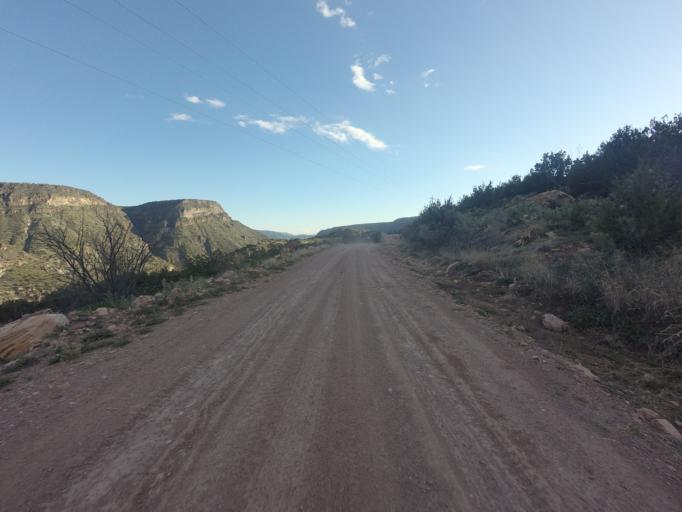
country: US
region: Arizona
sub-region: Gila County
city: Pine
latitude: 34.3726
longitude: -111.6640
